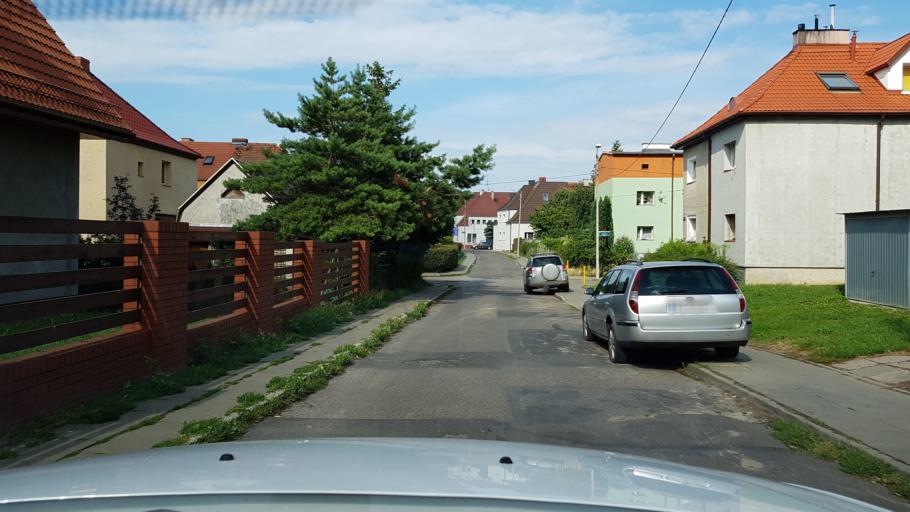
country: PL
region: West Pomeranian Voivodeship
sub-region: Szczecin
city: Szczecin
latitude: 53.4563
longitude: 14.5614
